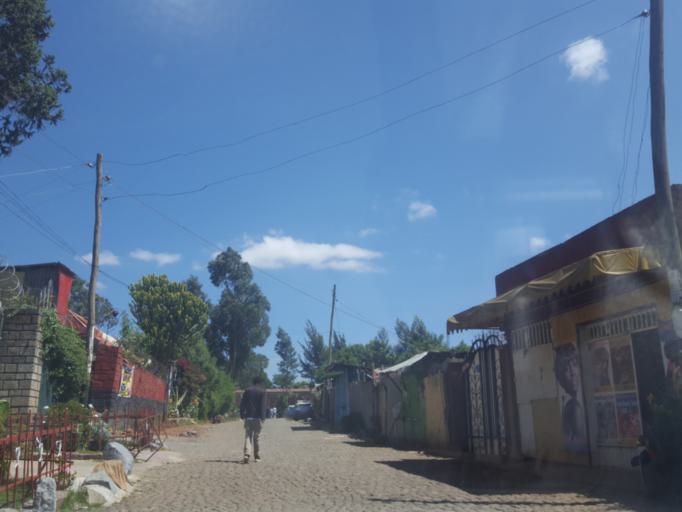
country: ET
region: Adis Abeba
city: Addis Ababa
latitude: 9.0571
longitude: 38.7407
